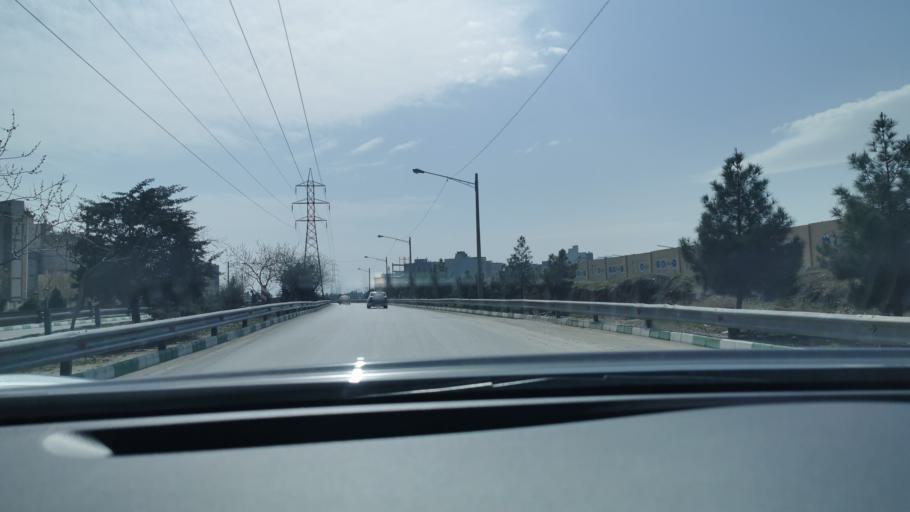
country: IR
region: Razavi Khorasan
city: Mashhad
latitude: 36.2846
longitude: 59.5410
